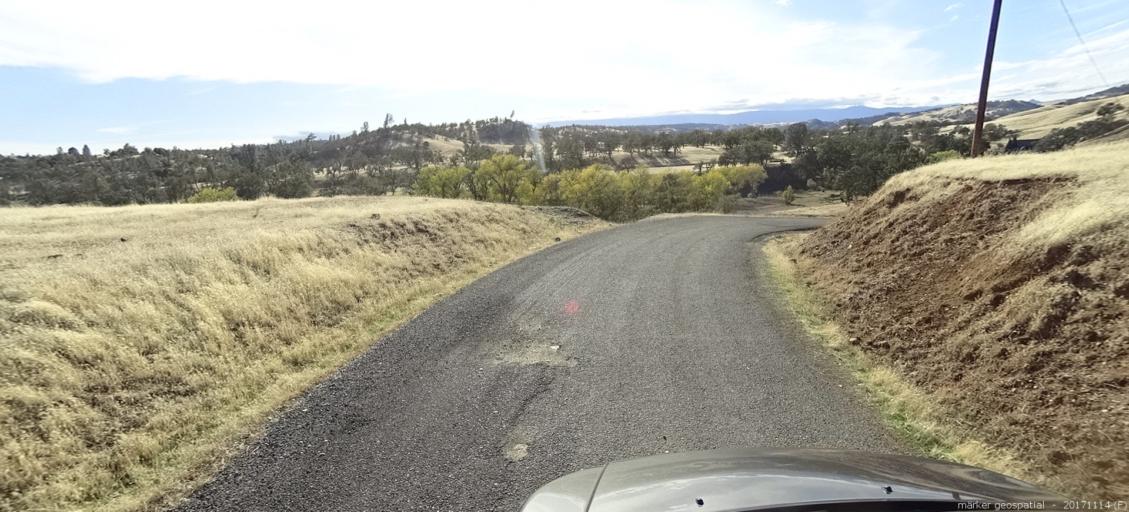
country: US
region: California
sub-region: Shasta County
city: Shasta
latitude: 40.3694
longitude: -122.5743
